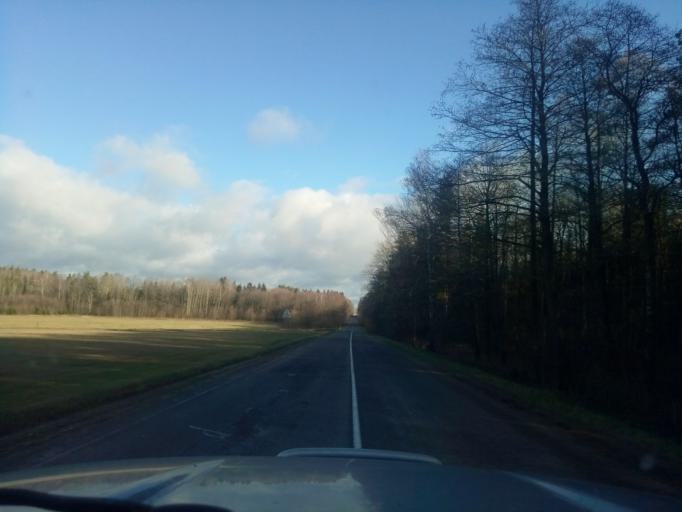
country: BY
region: Minsk
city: Tsimkavichy
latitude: 53.1693
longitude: 26.9221
